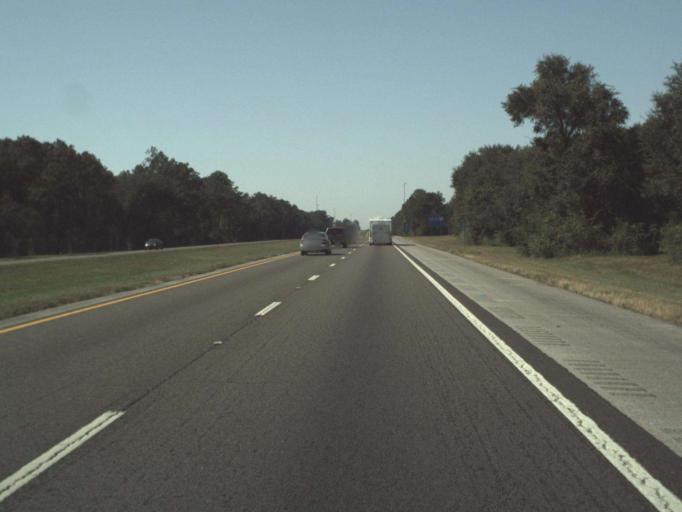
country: US
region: Florida
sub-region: Santa Rosa County
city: East Milton
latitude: 30.6234
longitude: -86.9497
